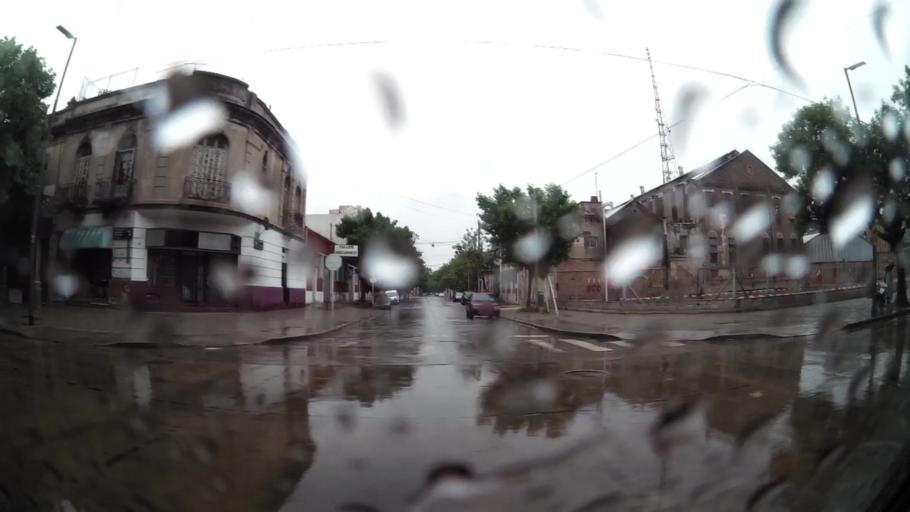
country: AR
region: Buenos Aires
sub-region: Partido de Avellaneda
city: Avellaneda
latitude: -34.6411
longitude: -58.3691
